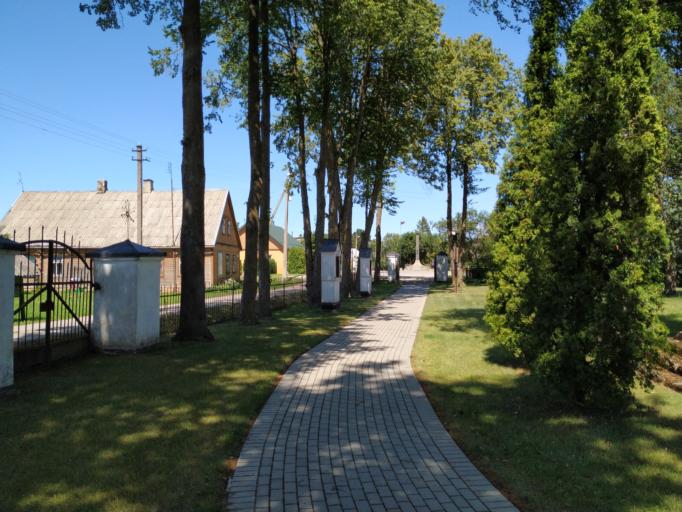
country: LT
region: Panevezys
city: Pasvalys
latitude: 56.2267
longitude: 24.4036
